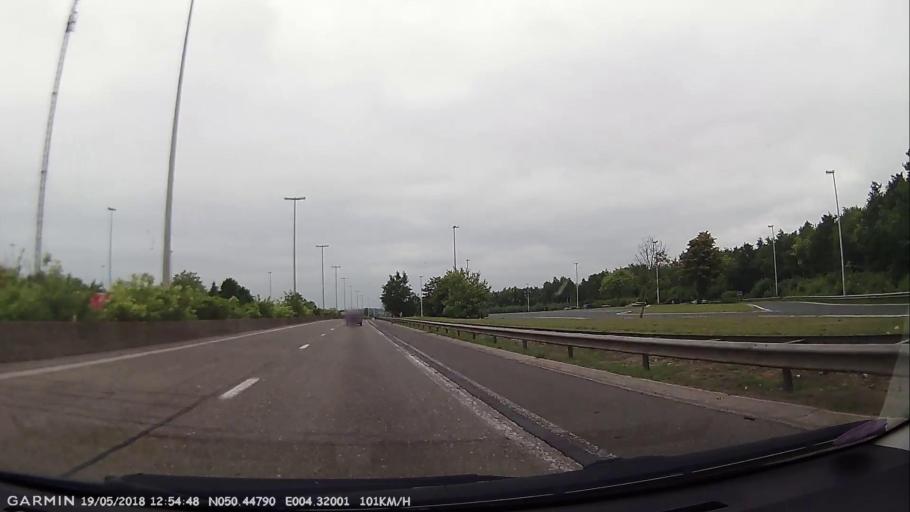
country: BE
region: Wallonia
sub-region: Province du Hainaut
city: Chapelle-lez-Herlaimont
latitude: 50.4481
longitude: 4.3197
